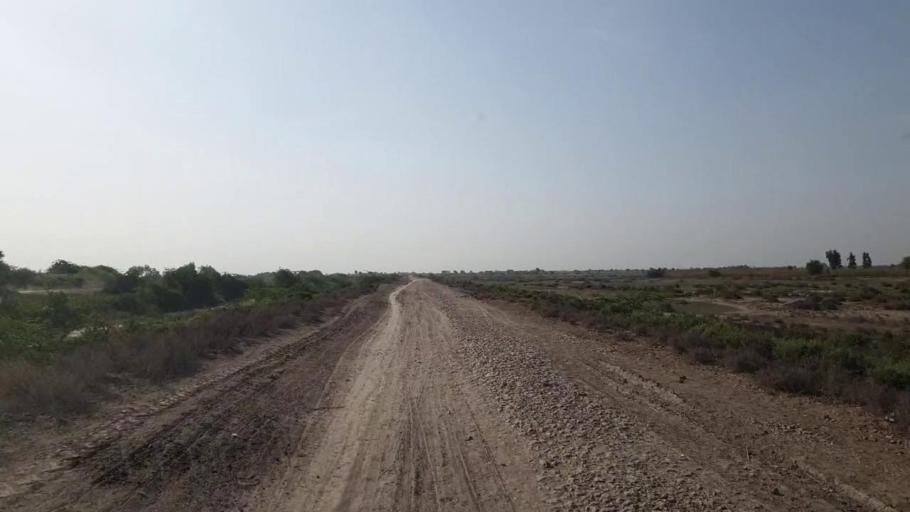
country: PK
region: Sindh
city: Kadhan
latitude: 24.6356
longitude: 69.0725
